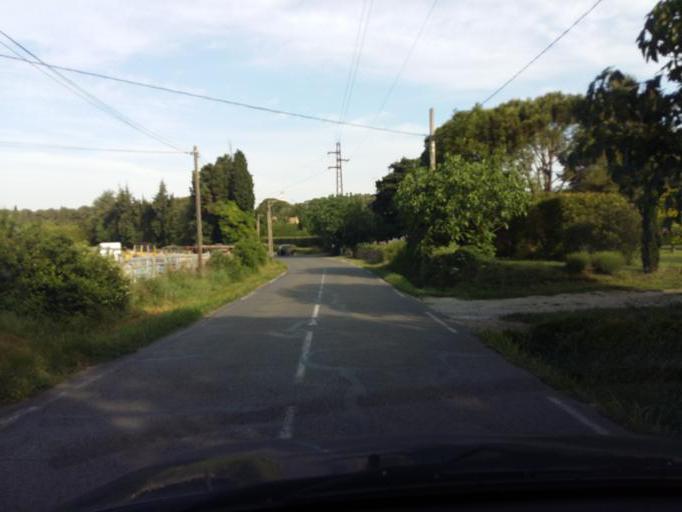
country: FR
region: Provence-Alpes-Cote d'Azur
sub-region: Departement des Bouches-du-Rhone
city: Pelissanne
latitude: 43.6352
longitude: 5.1284
